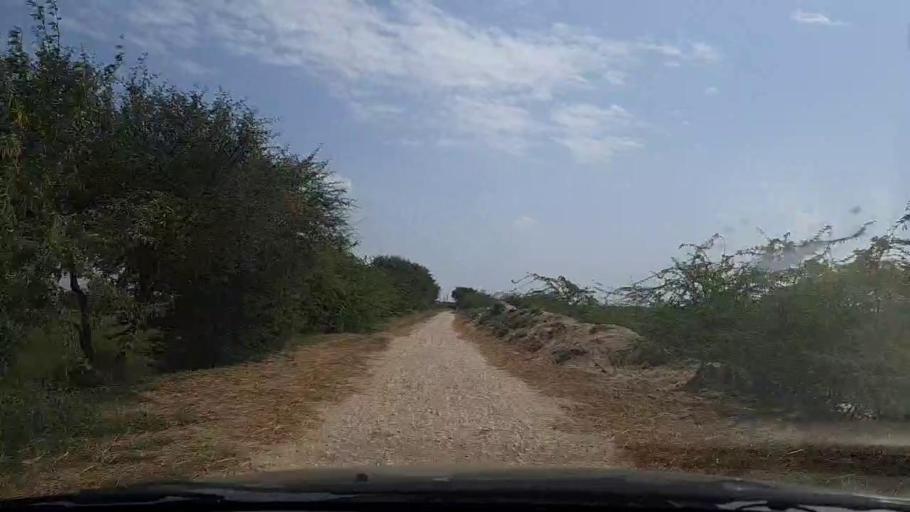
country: PK
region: Sindh
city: Mirpur Batoro
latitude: 24.5715
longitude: 68.1973
